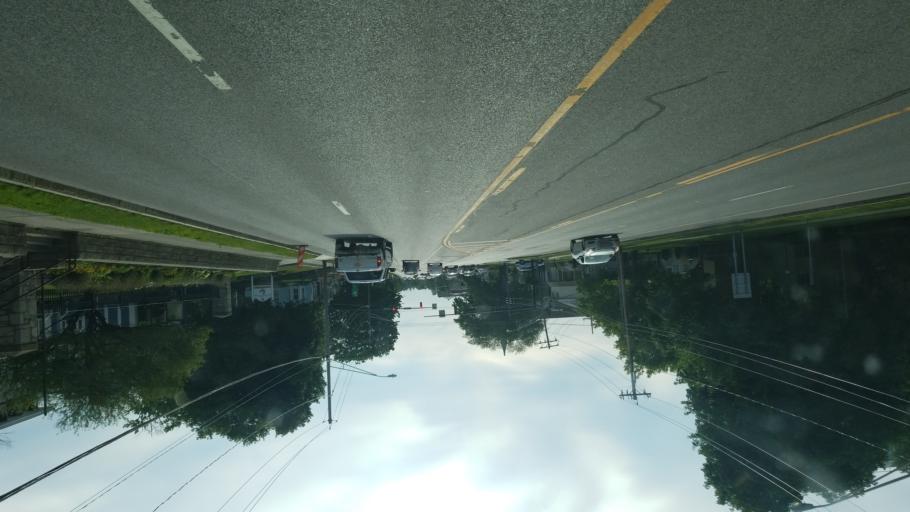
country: US
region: New York
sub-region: Genesee County
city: Batavia
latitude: 42.9965
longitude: -78.1755
